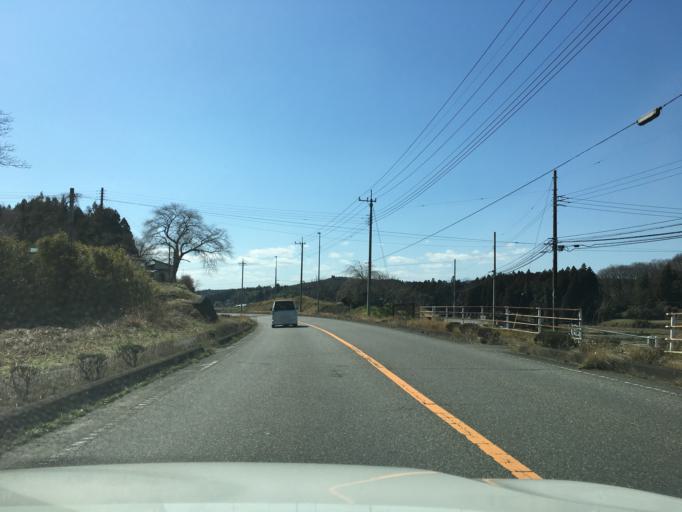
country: JP
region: Tochigi
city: Kuroiso
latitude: 36.9521
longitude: 140.1518
